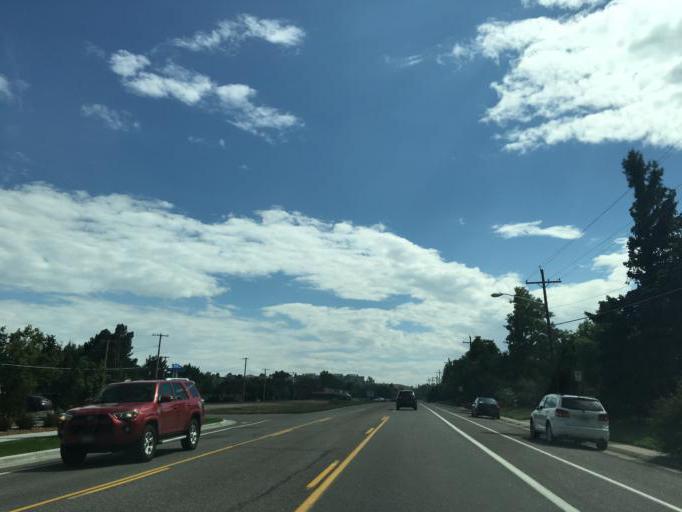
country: US
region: Colorado
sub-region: Jefferson County
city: Applewood
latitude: 39.7507
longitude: -105.1424
